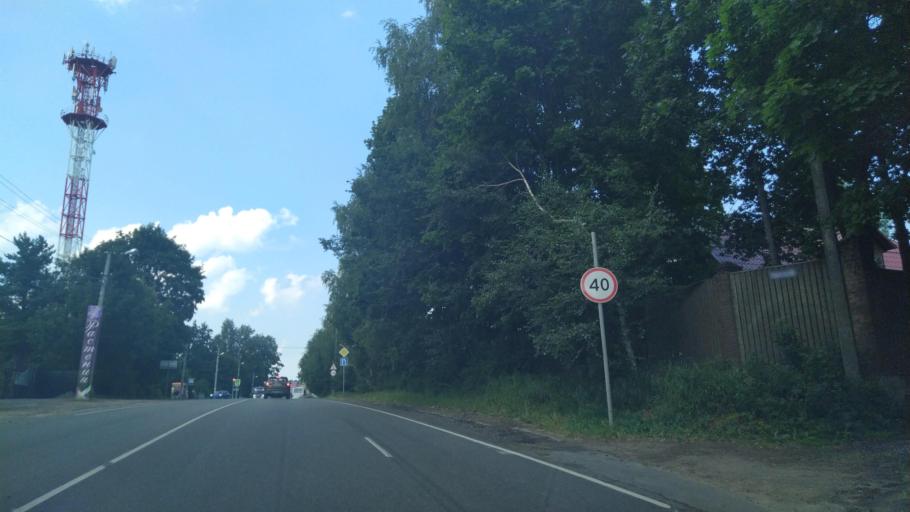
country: RU
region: Leningrad
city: Toksovo
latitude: 60.1596
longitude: 30.5353
